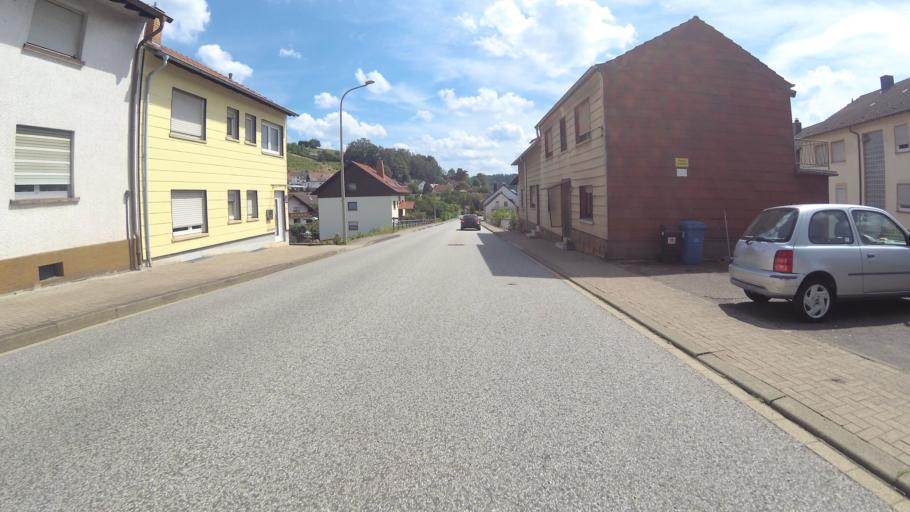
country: DE
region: Rheinland-Pfalz
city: Bann
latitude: 49.3977
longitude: 7.6107
